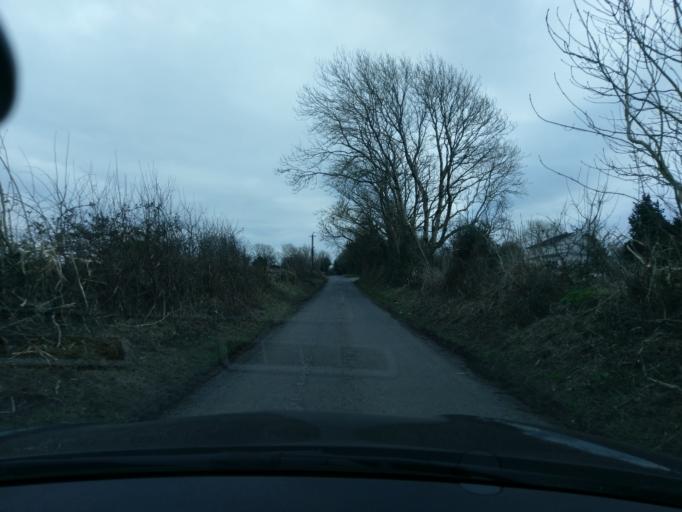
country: IE
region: Connaught
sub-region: County Galway
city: Oranmore
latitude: 53.1731
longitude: -8.8914
